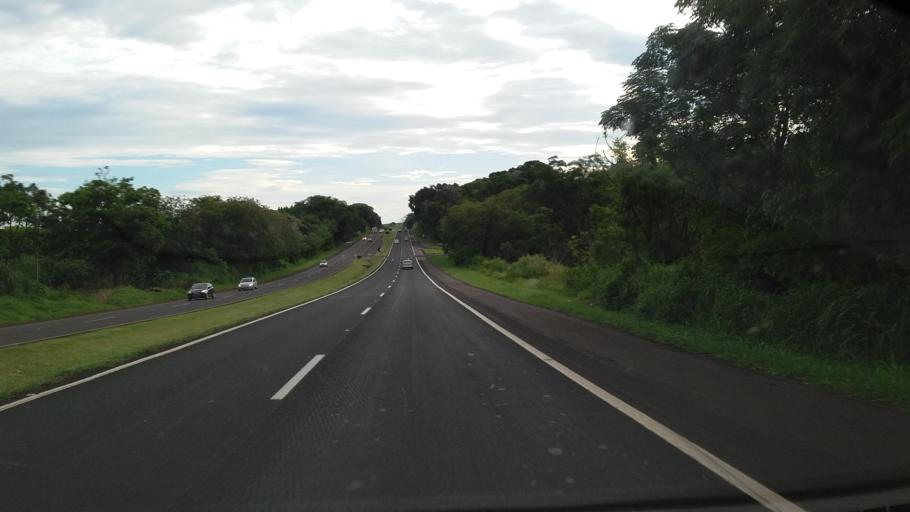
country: BR
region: Parana
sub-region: Paicandu
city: Paicandu
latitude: -23.5030
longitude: -52.0189
